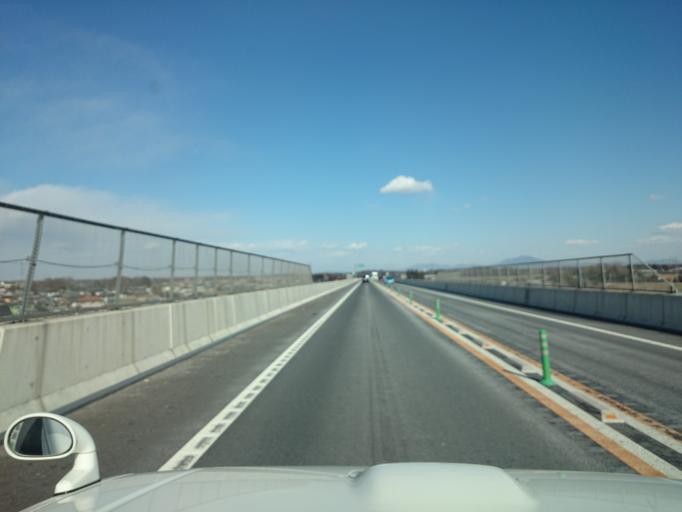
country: JP
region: Ibaraki
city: Sakai
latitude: 36.1197
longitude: 139.7725
